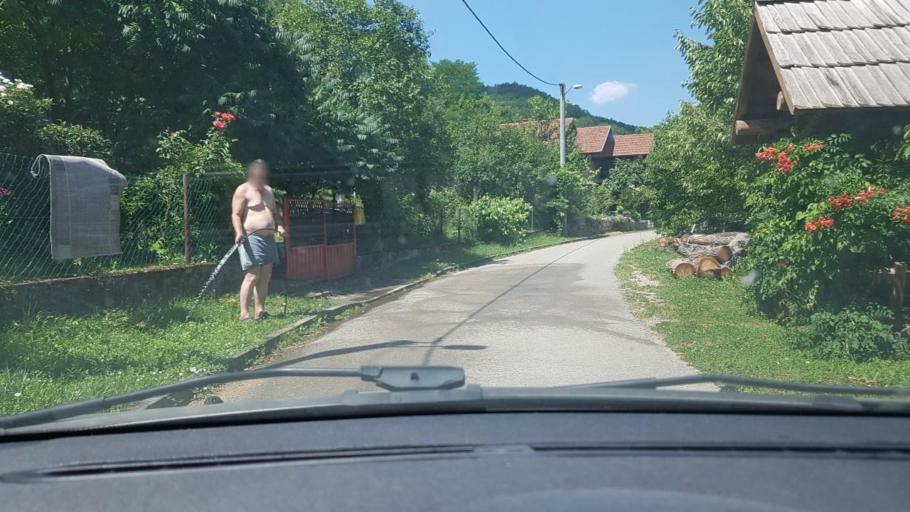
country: BA
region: Federation of Bosnia and Herzegovina
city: Orasac
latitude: 44.5605
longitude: 16.0849
